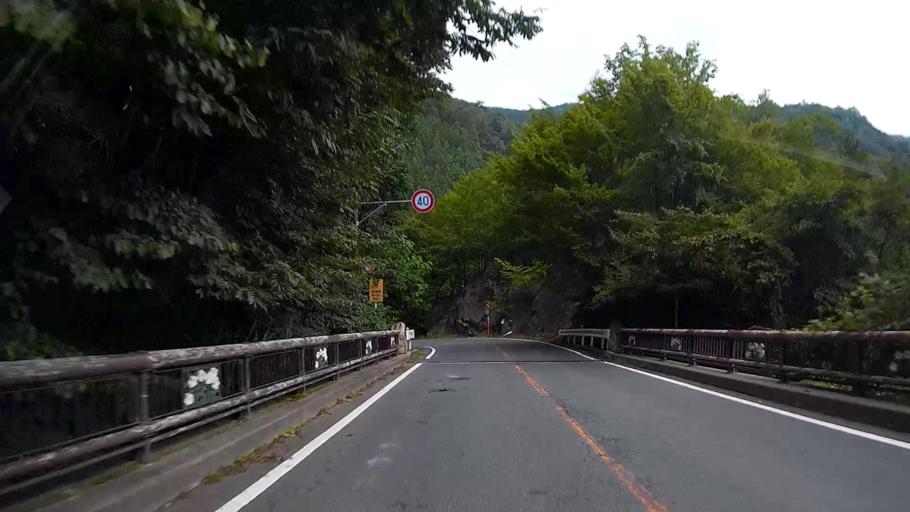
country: JP
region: Yamanashi
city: Enzan
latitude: 35.9225
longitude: 138.8290
